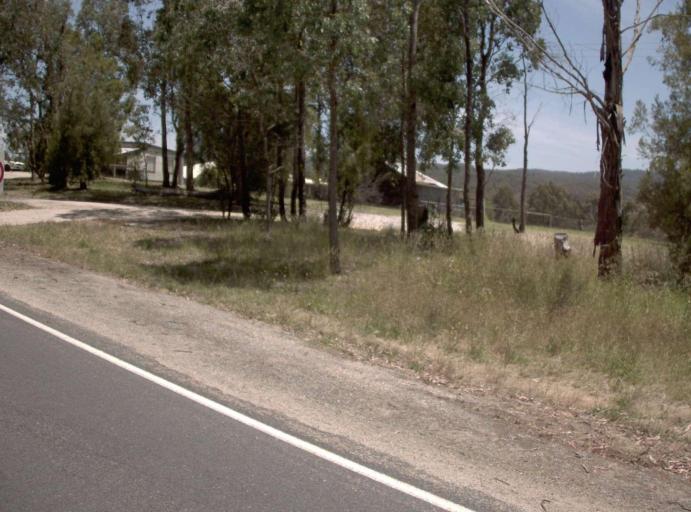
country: AU
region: Victoria
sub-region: East Gippsland
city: Lakes Entrance
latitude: -37.6845
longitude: 147.8423
